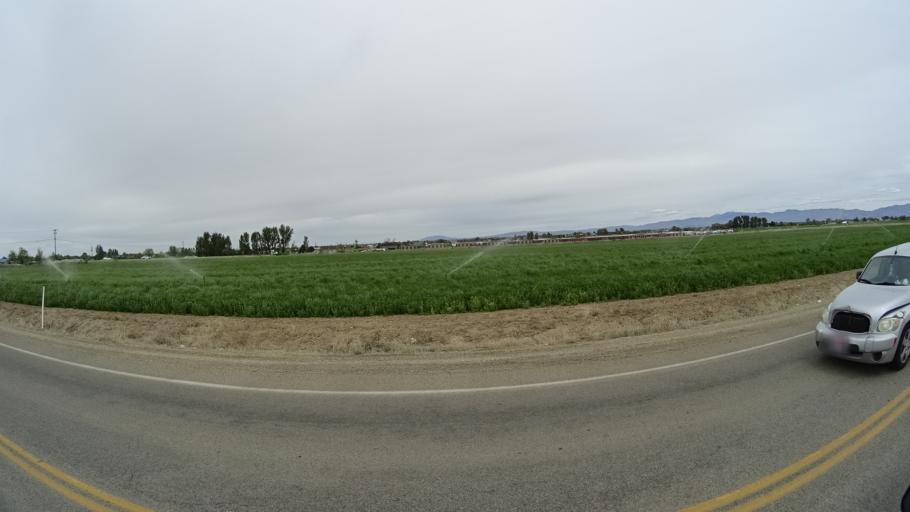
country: US
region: Idaho
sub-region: Ada County
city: Kuna
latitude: 43.4878
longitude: -116.3927
